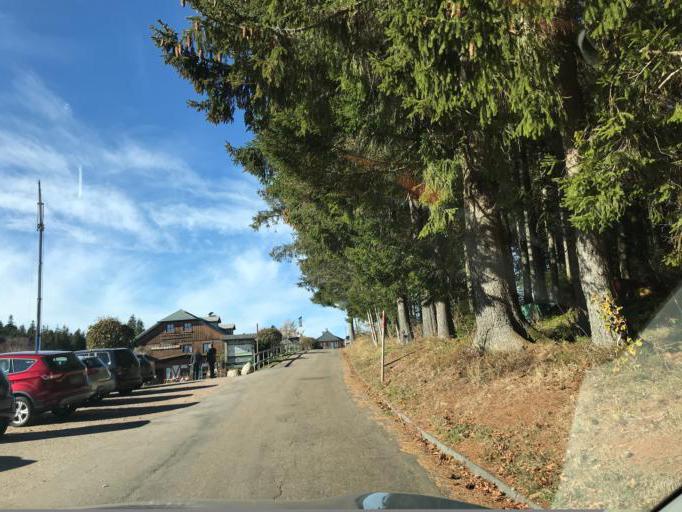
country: DE
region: Baden-Wuerttemberg
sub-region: Freiburg Region
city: Gutenbach
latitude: 48.0955
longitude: 8.1568
